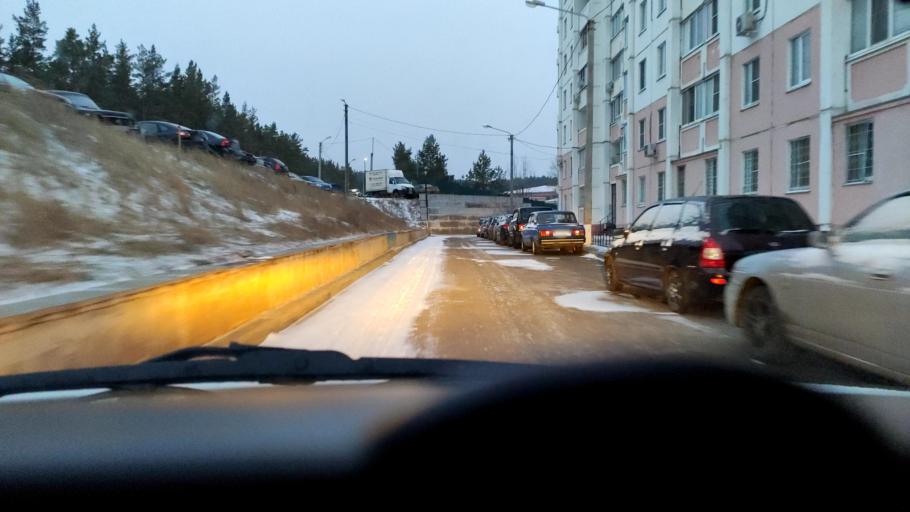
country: RU
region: Voronezj
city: Pridonskoy
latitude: 51.7059
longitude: 39.1077
